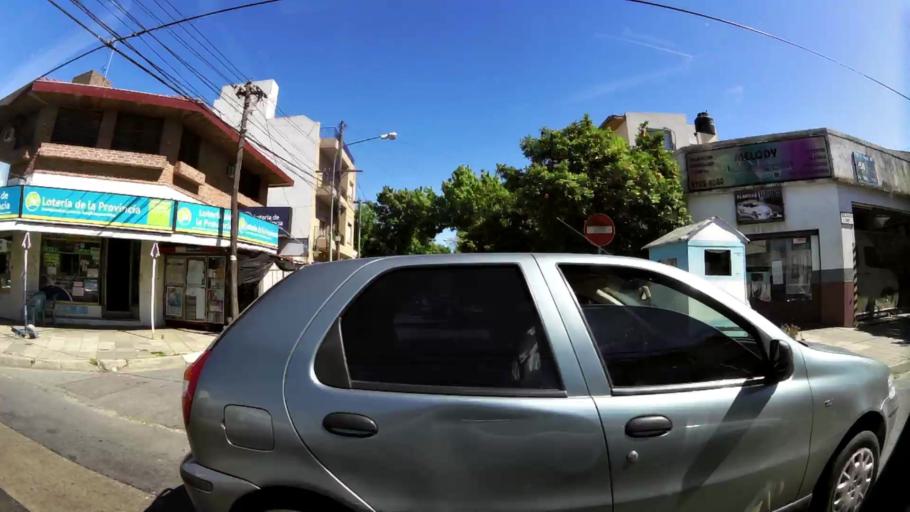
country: AR
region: Buenos Aires
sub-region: Partido de Vicente Lopez
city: Olivos
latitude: -34.5276
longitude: -58.5054
